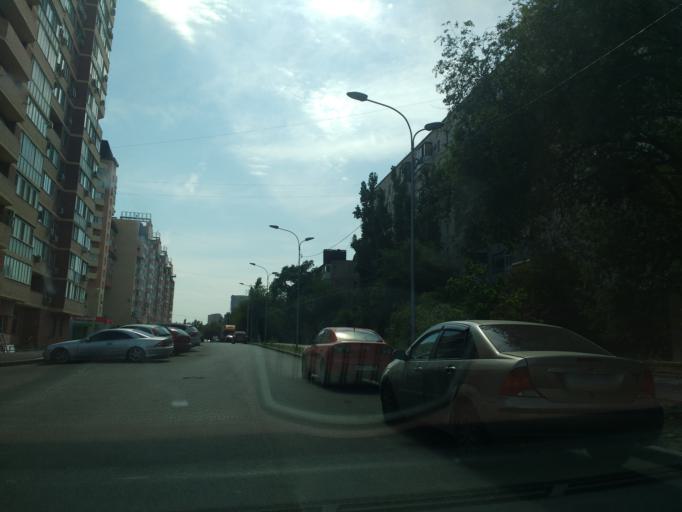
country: RU
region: Volgograd
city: Volgograd
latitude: 48.6909
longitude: 44.4943
